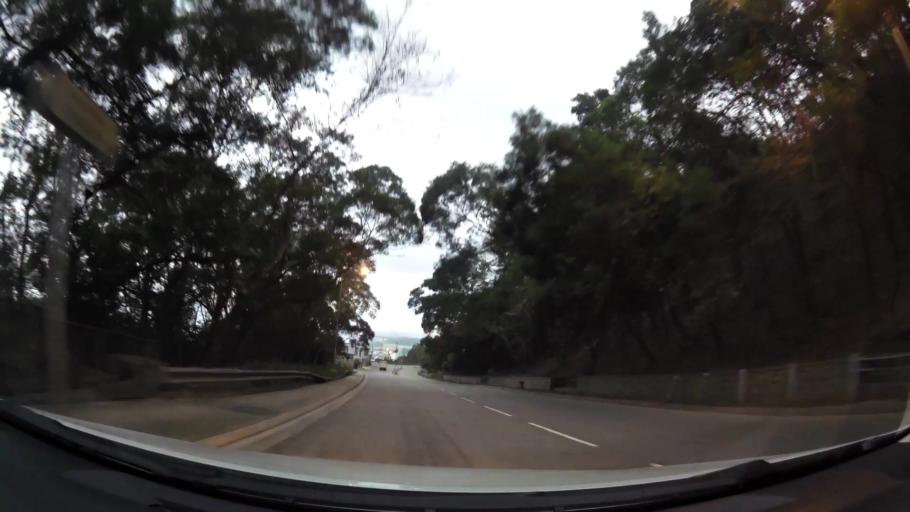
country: HK
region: Tsuen Wan
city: Tsuen Wan
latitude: 22.3313
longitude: 114.0923
